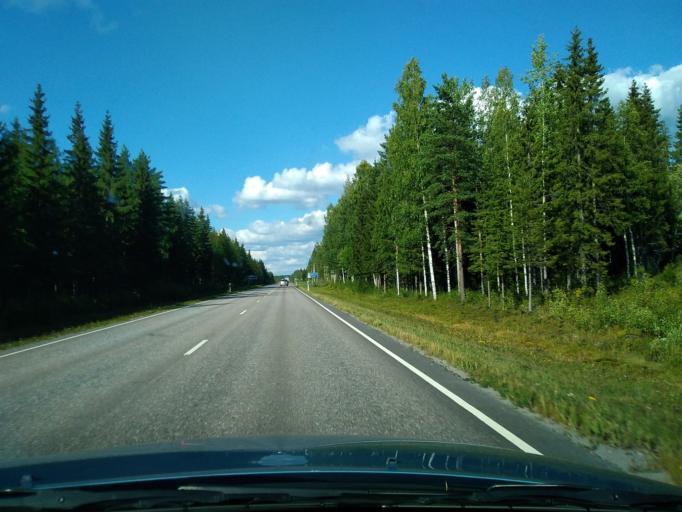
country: FI
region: Pirkanmaa
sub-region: Ylae-Pirkanmaa
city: Maenttae
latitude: 62.0391
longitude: 24.7098
